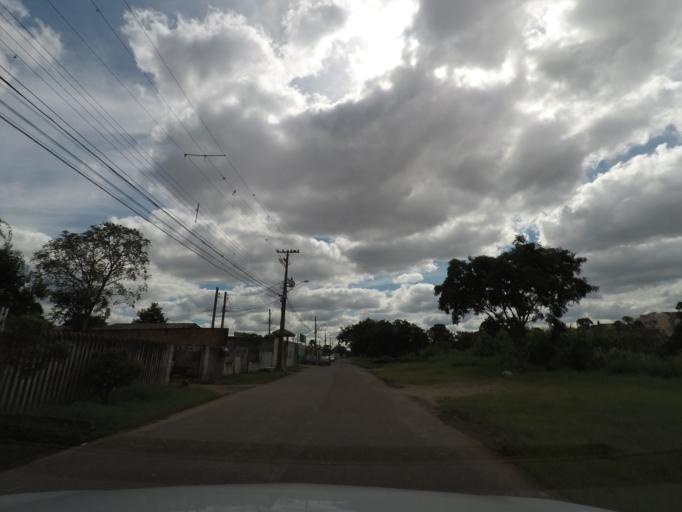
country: BR
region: Parana
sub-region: Sao Jose Dos Pinhais
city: Sao Jose dos Pinhais
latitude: -25.4878
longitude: -49.2332
